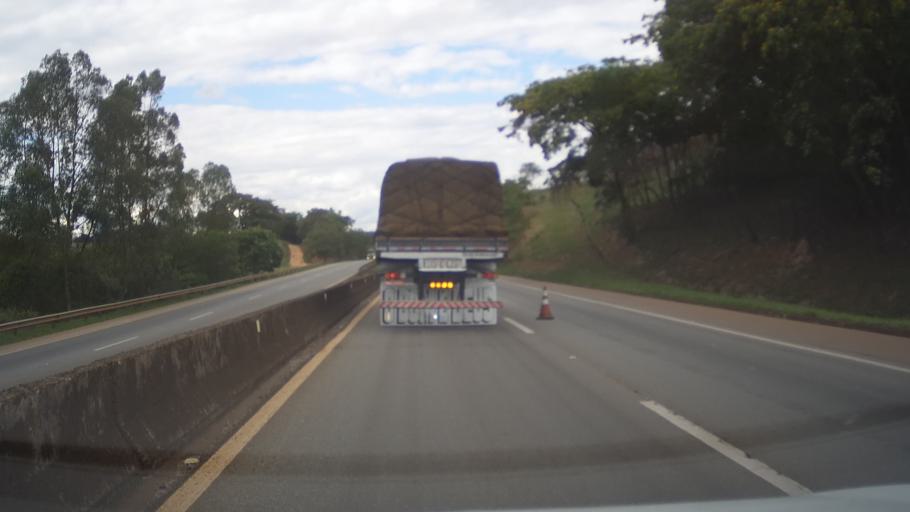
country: BR
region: Minas Gerais
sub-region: Itauna
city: Itauna
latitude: -20.3146
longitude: -44.4523
